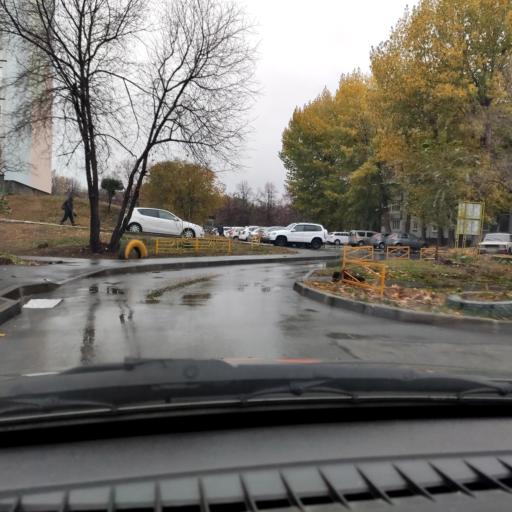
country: RU
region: Samara
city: Tol'yatti
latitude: 53.5205
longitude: 49.2879
